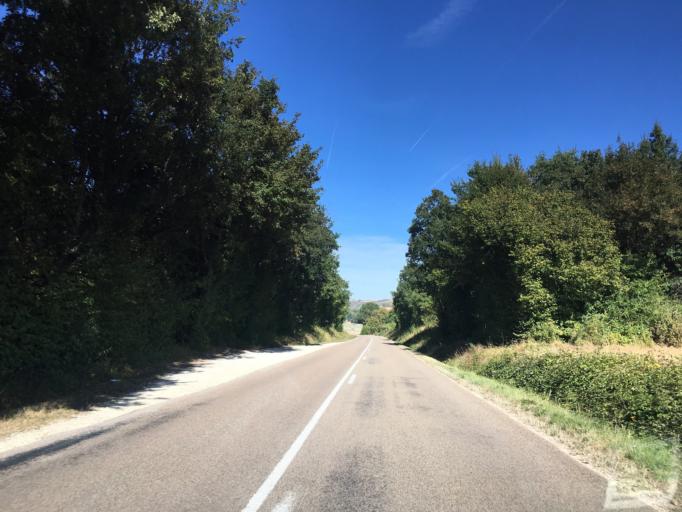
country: FR
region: Bourgogne
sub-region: Departement de l'Yonne
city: Saint-Bris-le-Vineux
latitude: 47.6842
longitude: 3.6537
